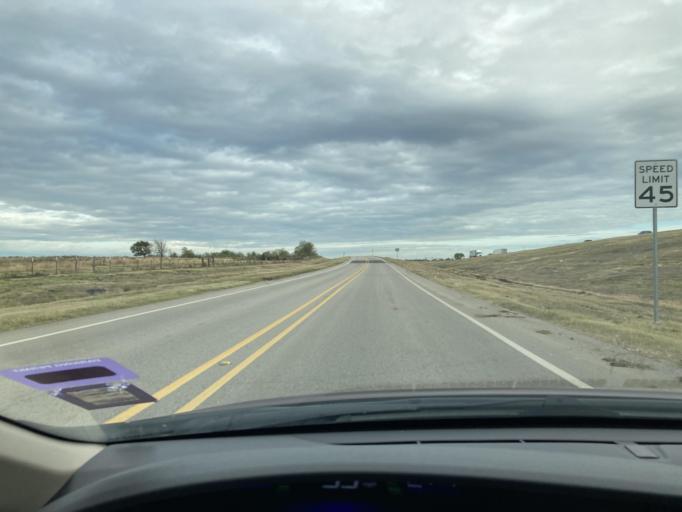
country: US
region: Texas
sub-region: Navarro County
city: Corsicana
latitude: 32.0482
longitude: -96.4954
